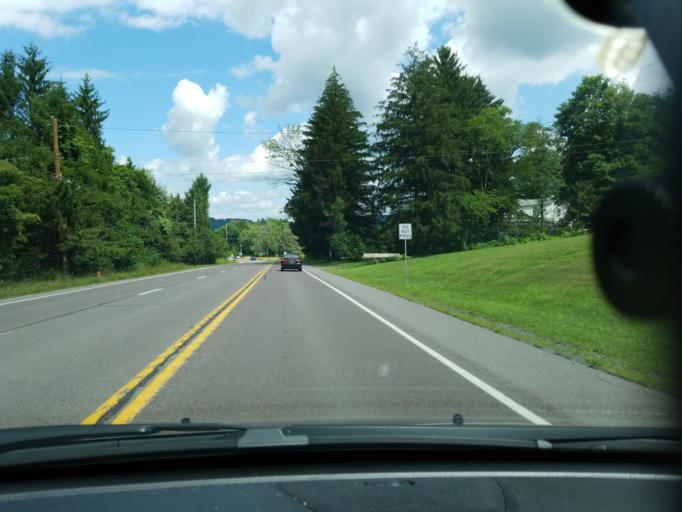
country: US
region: Pennsylvania
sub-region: Northumberland County
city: Elysburg
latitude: 40.8530
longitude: -76.5419
